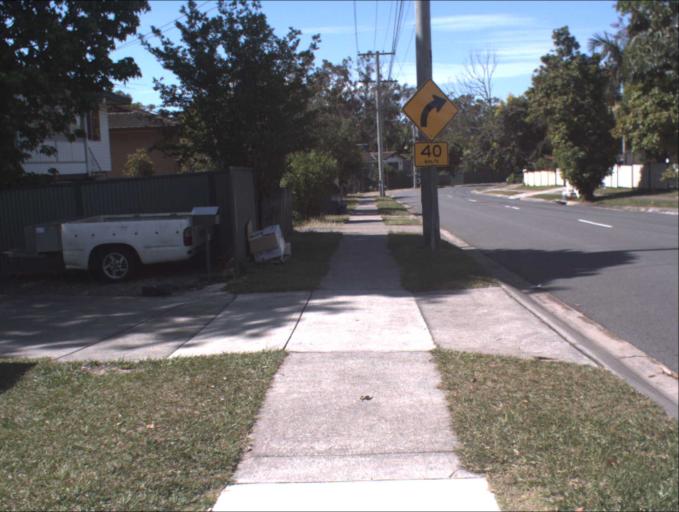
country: AU
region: Queensland
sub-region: Logan
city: Logan City
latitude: -27.6443
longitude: 153.1283
